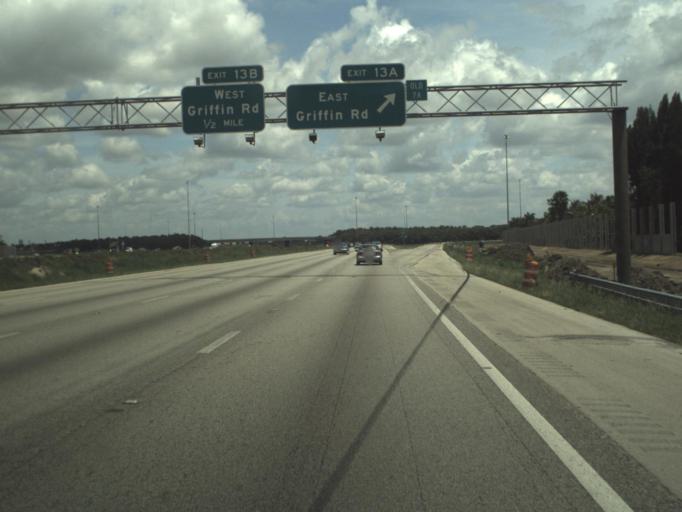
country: US
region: Florida
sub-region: Broward County
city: Southwest Ranches
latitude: 26.0551
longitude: -80.3527
